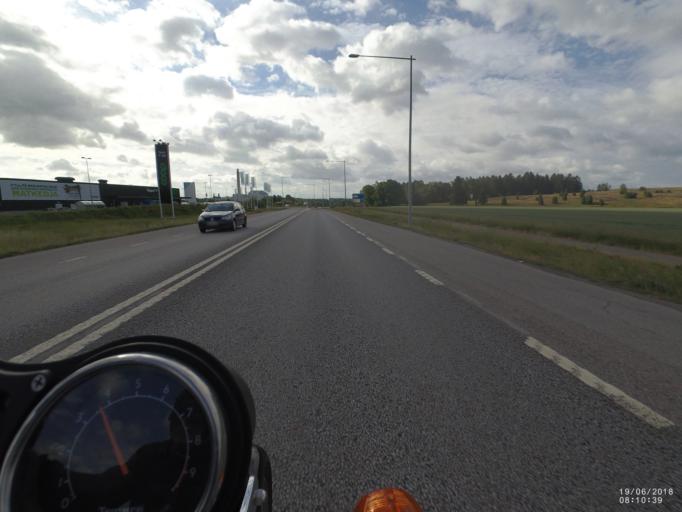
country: SE
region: Soedermanland
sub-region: Nykopings Kommun
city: Nykoping
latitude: 58.7470
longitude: 16.9910
